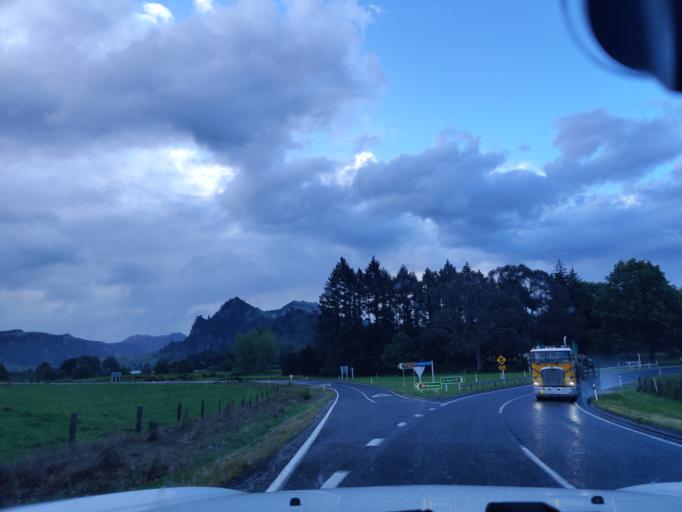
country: NZ
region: Waikato
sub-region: South Waikato District
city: Tokoroa
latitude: -38.4178
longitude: 175.8112
